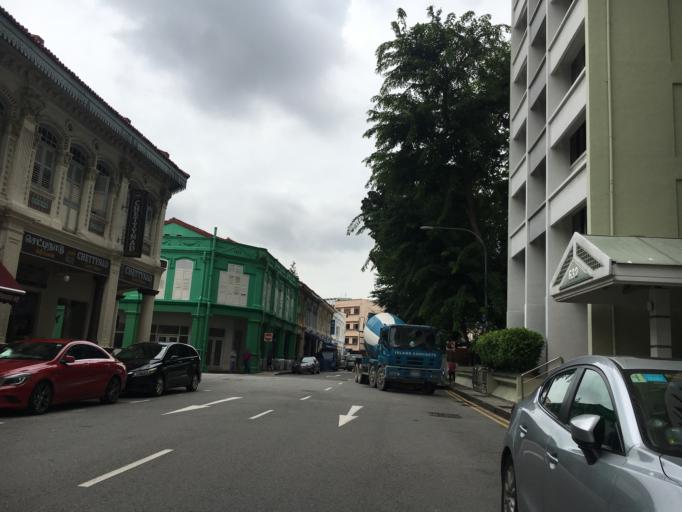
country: SG
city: Singapore
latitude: 1.3060
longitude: 103.8546
